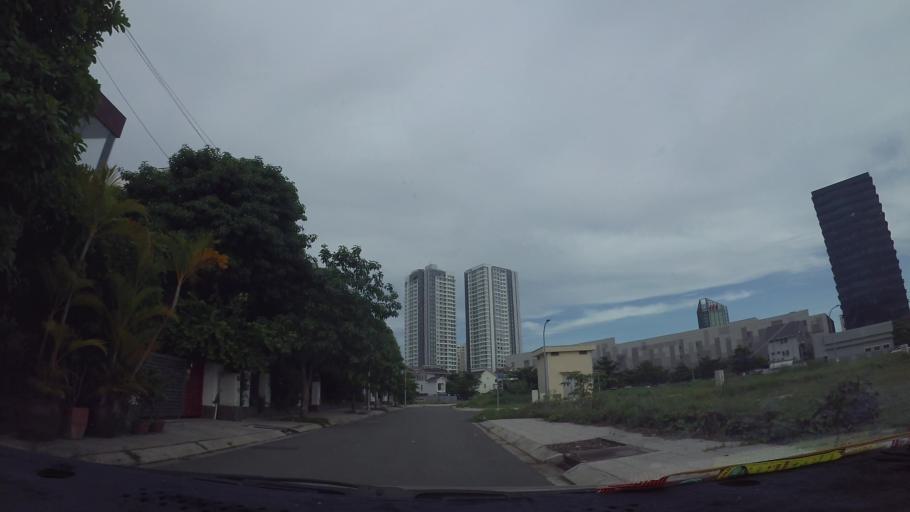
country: VN
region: Ho Chi Minh City
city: Quan Sau
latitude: 10.7437
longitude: 106.6510
